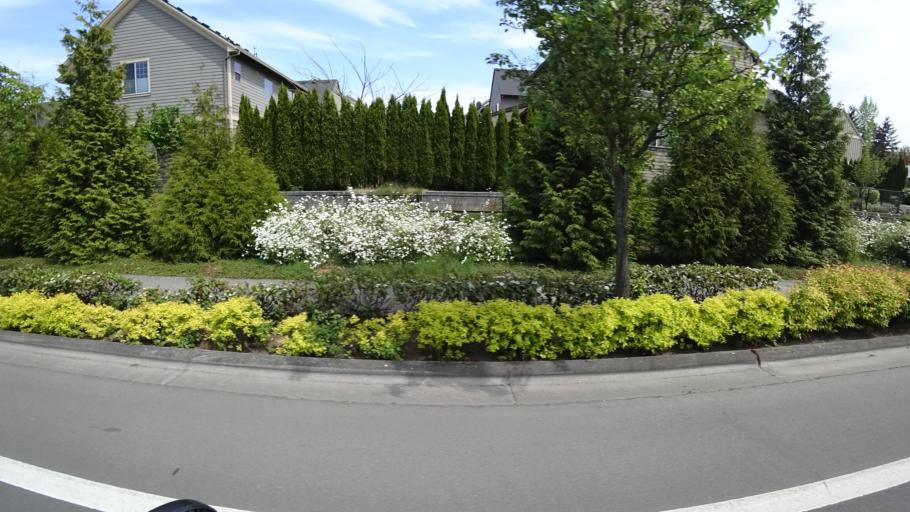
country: US
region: Oregon
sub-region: Washington County
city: Aloha
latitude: 45.4798
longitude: -122.8515
